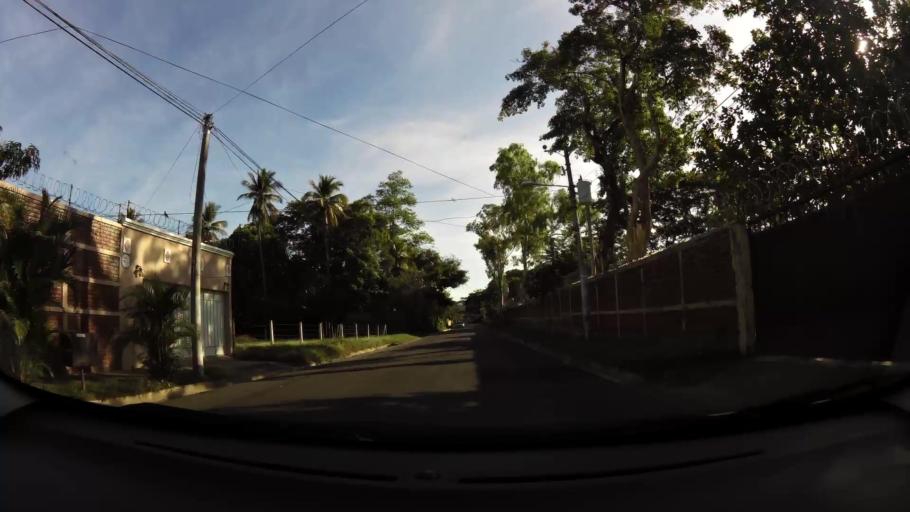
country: SV
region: San Miguel
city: San Miguel
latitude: 13.4717
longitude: -88.1852
